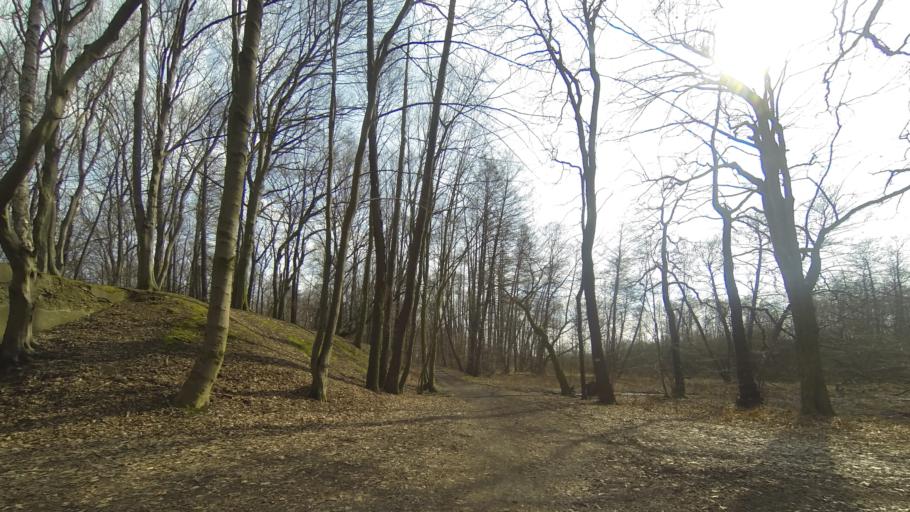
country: DE
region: Saxony
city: Radeburg
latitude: 51.2322
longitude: 13.7065
